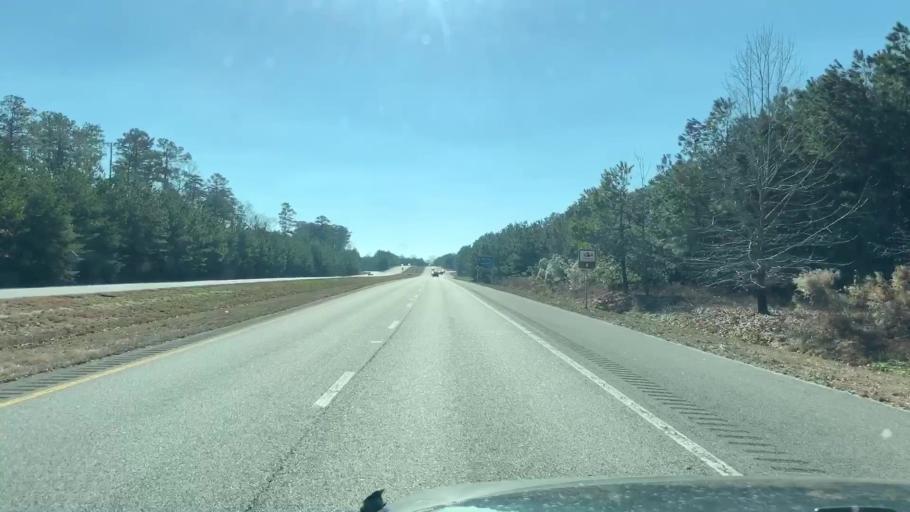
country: US
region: Virginia
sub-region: James City County
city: Williamsburg
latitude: 37.2798
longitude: -76.7535
